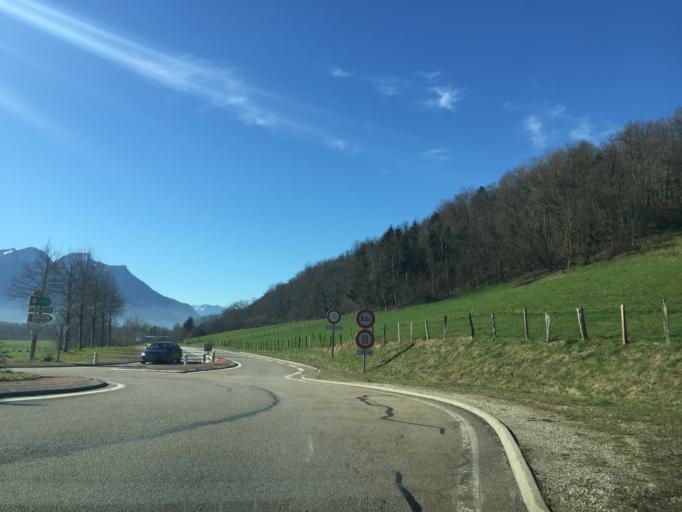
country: FR
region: Rhone-Alpes
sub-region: Departement de la Savoie
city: Les Echelles
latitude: 45.4462
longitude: 5.7637
